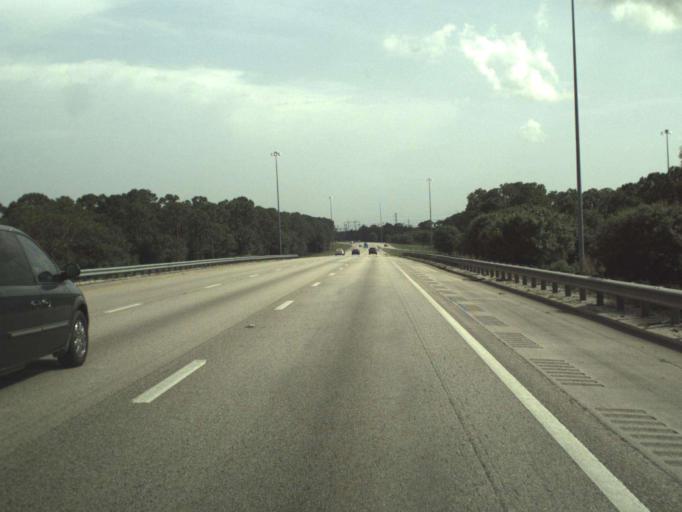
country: US
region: Florida
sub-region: Saint Lucie County
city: Fort Pierce South
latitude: 27.3736
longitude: -80.4108
